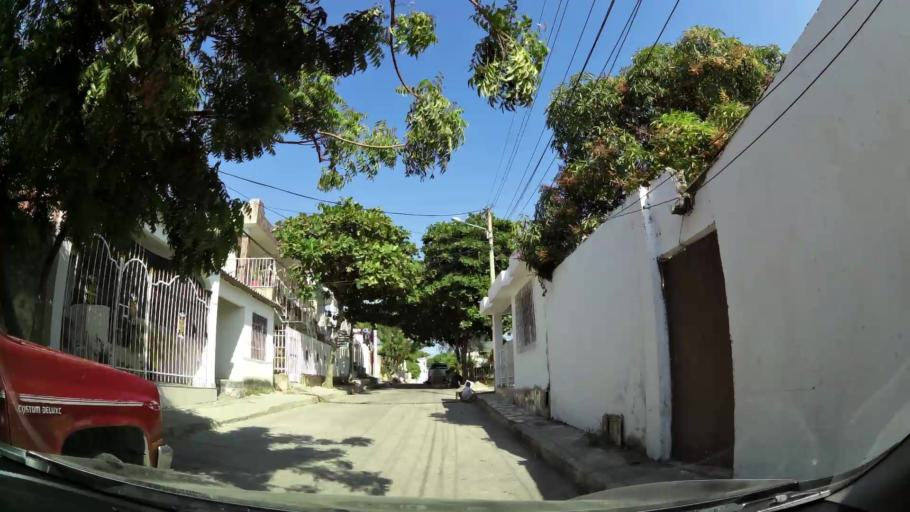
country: CO
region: Bolivar
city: Cartagena
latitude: 10.3940
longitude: -75.5020
